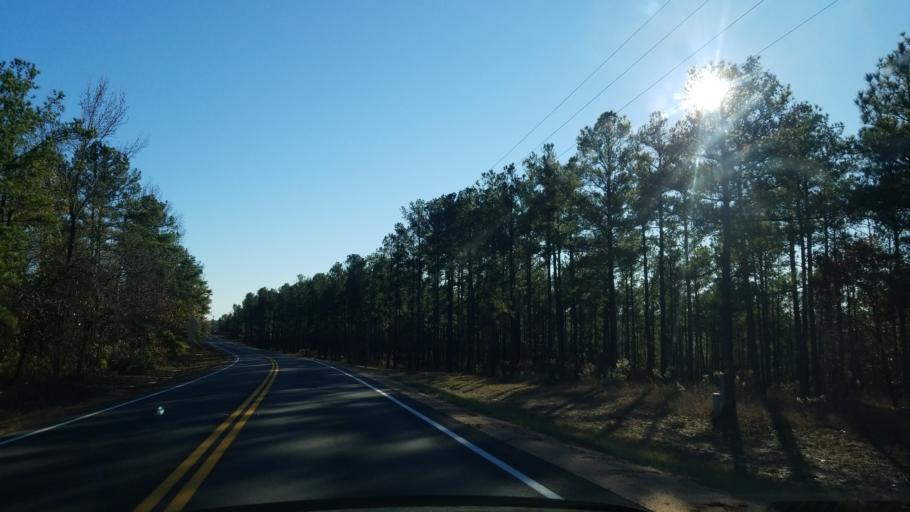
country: US
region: Georgia
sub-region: Talbot County
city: Talbotton
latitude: 32.5727
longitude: -84.5415
